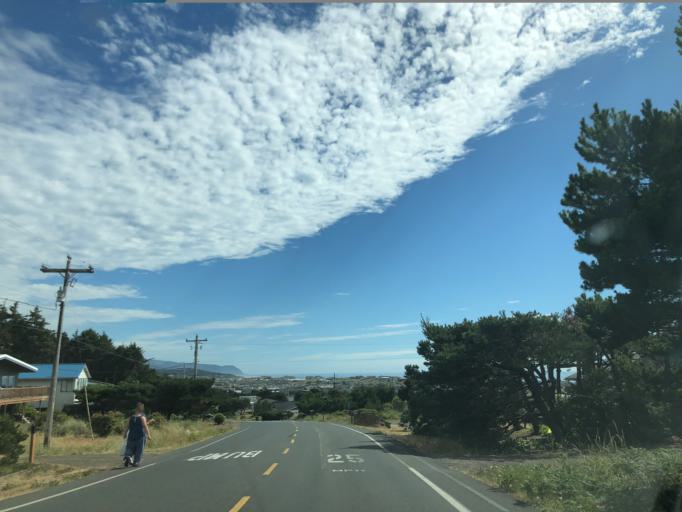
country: US
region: Oregon
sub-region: Lincoln County
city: Waldport
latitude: 44.4398
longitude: -124.0785
